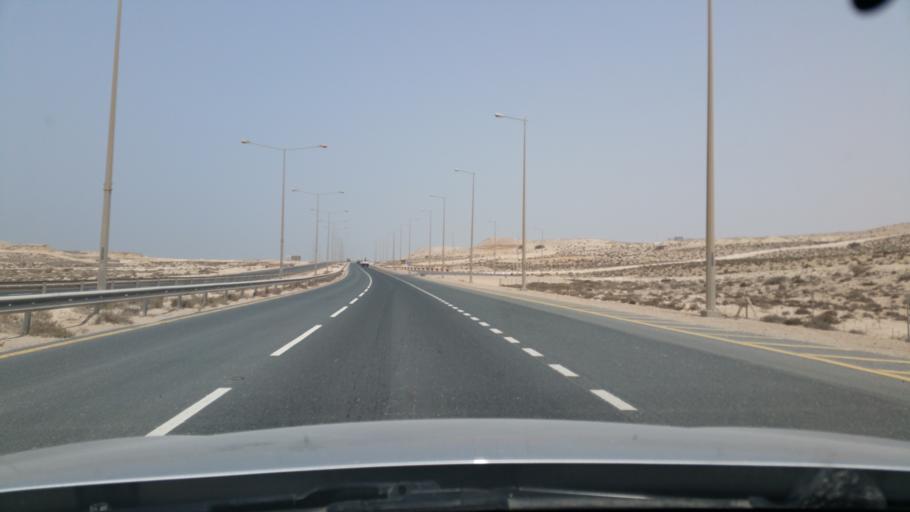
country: QA
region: Baladiyat ar Rayyan
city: Dukhan
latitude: 25.3481
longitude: 50.7823
